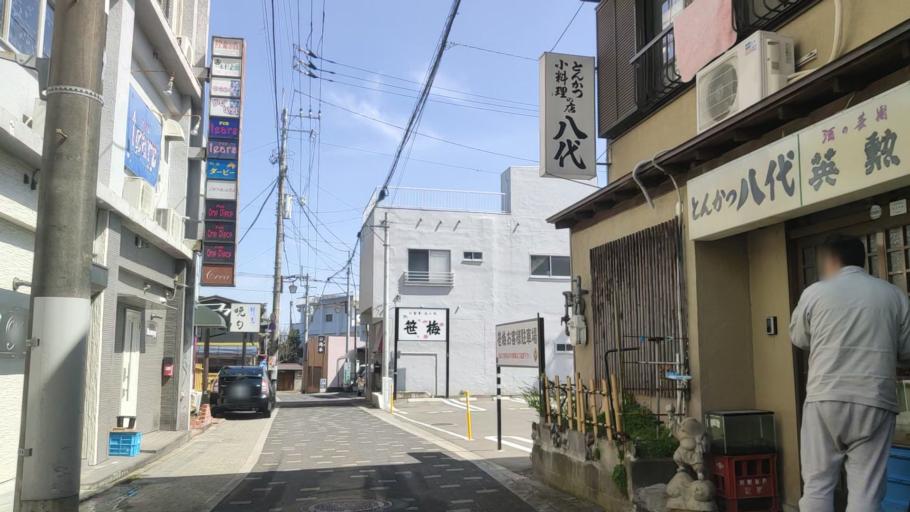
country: JP
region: Yamanashi
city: Fujikawaguchiko
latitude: 35.4924
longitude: 138.8014
